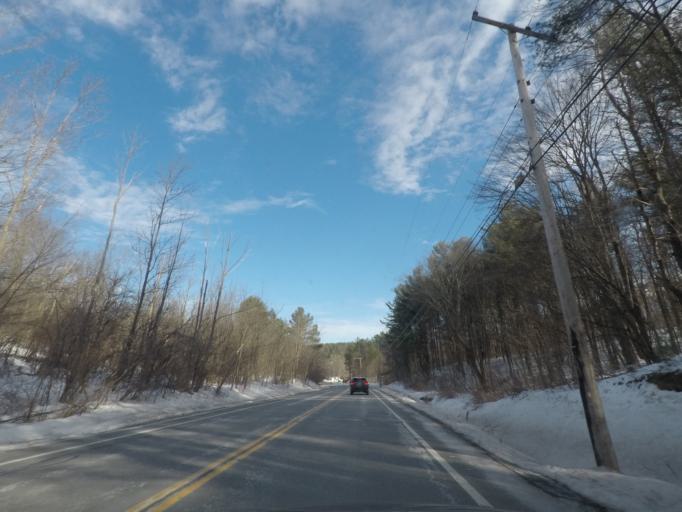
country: US
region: New York
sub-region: Albany County
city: Altamont
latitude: 42.7730
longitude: -74.0839
